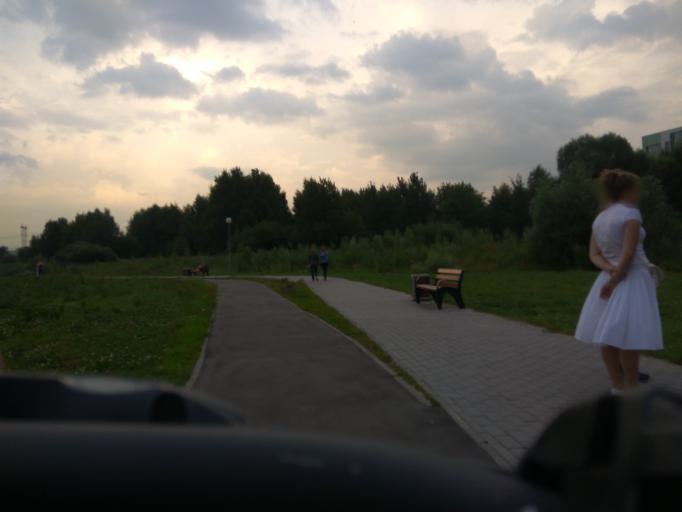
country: RU
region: Moscow
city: Brateyevo
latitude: 55.6301
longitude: 37.7671
